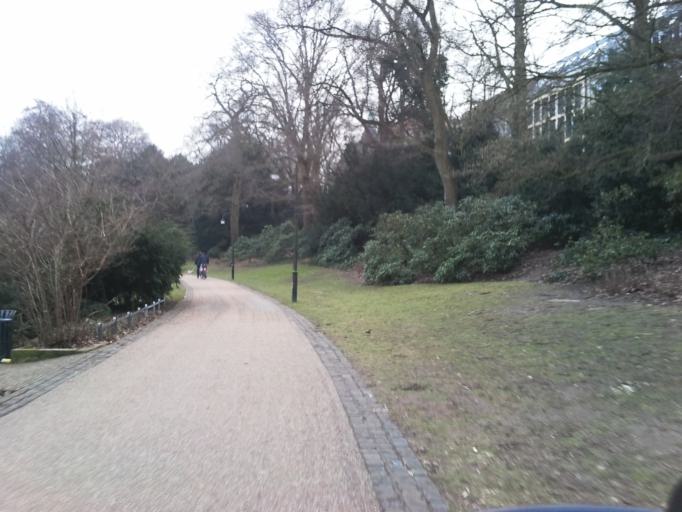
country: DE
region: Bremen
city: Bremen
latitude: 53.0757
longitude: 8.8131
